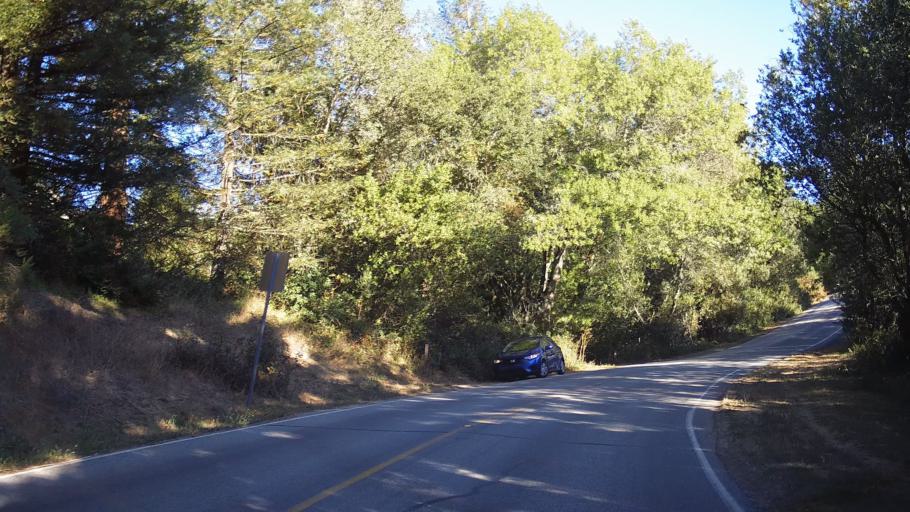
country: US
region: California
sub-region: Contra Costa County
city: Orinda
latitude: 37.8825
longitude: -122.2263
